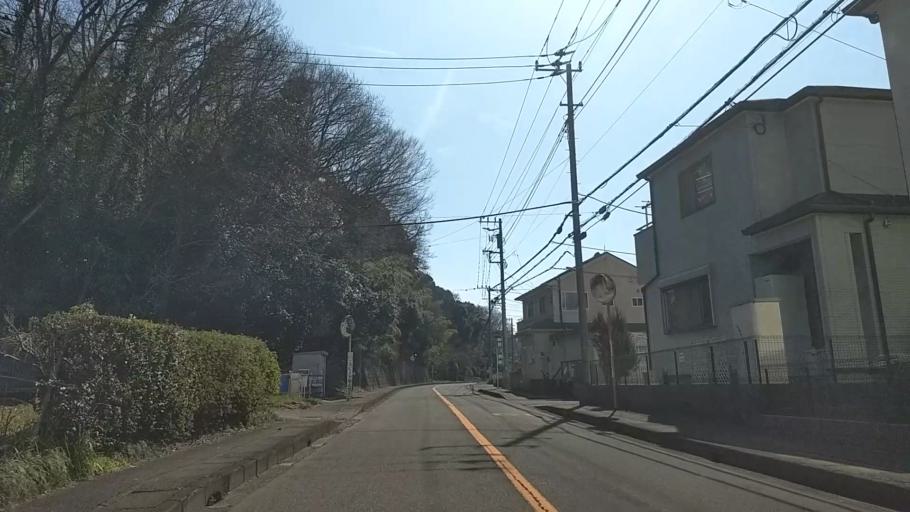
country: JP
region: Kanagawa
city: Fujisawa
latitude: 35.3755
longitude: 139.4282
